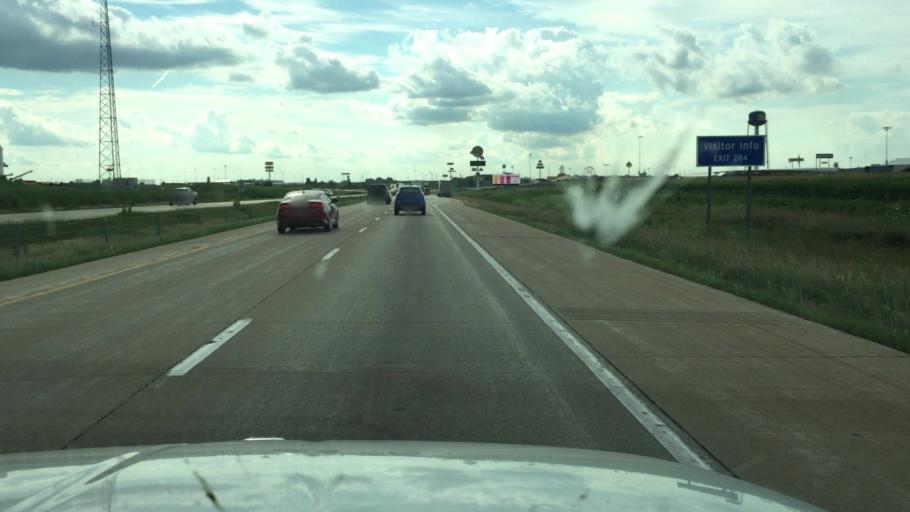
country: US
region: Iowa
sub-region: Scott County
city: Walcott
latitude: 41.6142
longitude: -90.7710
